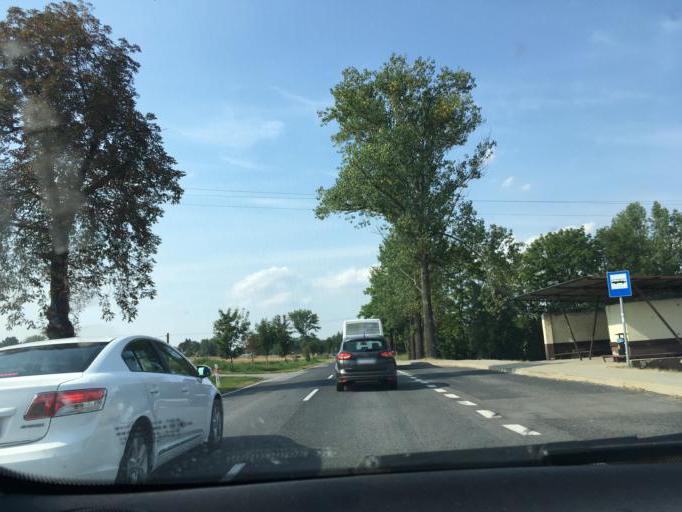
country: PL
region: Opole Voivodeship
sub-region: Powiat prudnicki
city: Laka Prudnicka
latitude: 50.3762
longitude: 17.5338
